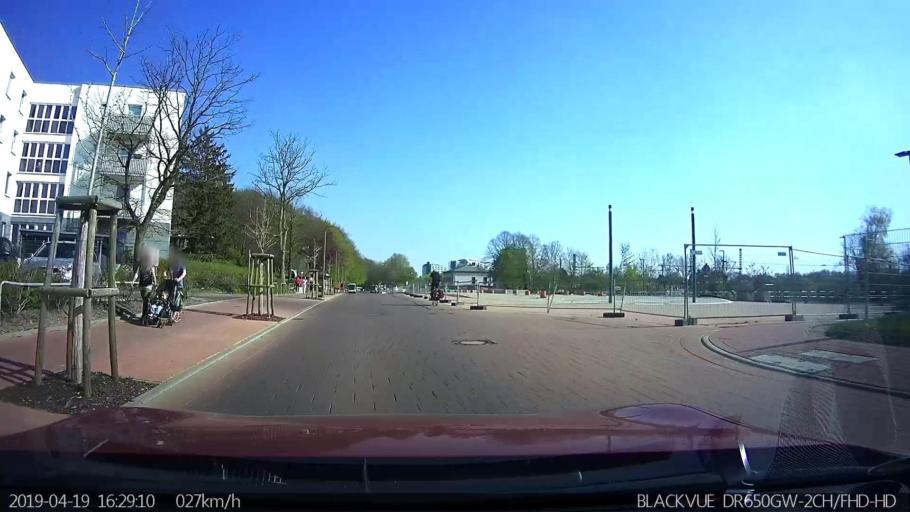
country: DE
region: Schleswig-Holstein
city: Pinneberg
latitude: 53.6568
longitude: 9.7962
